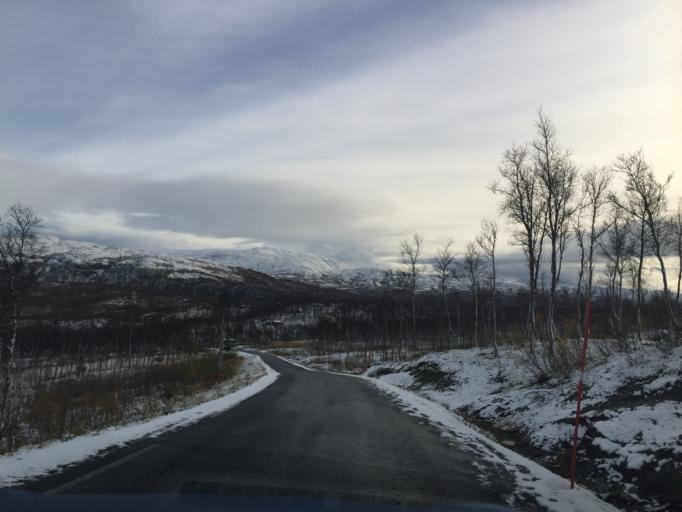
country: NO
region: Nordland
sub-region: Sorfold
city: Straumen
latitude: 67.0869
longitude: 16.0212
